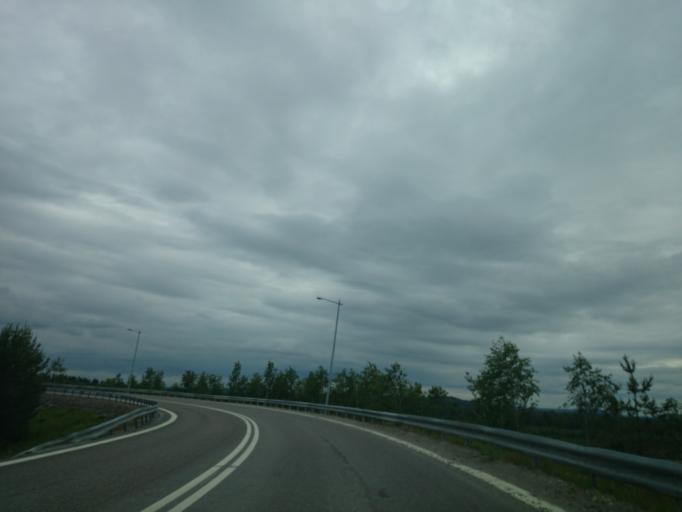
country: SE
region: Vaesternorrland
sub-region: Timra Kommun
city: Soraker
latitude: 62.5270
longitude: 17.4746
